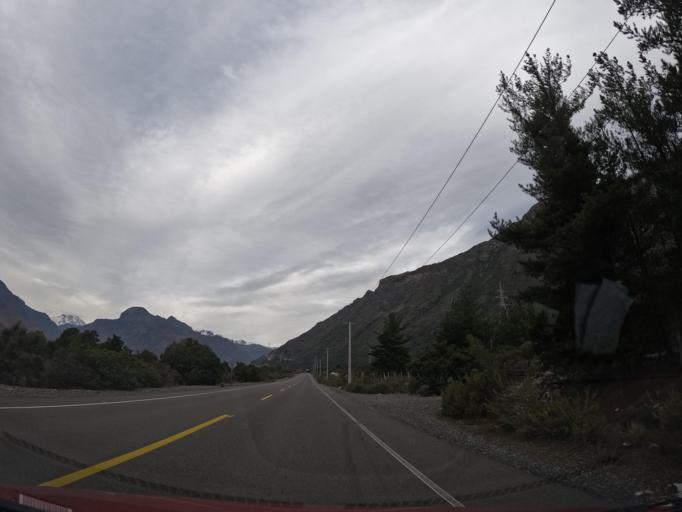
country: CL
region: Maule
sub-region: Provincia de Linares
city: Colbun
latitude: -35.7093
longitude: -71.0979
